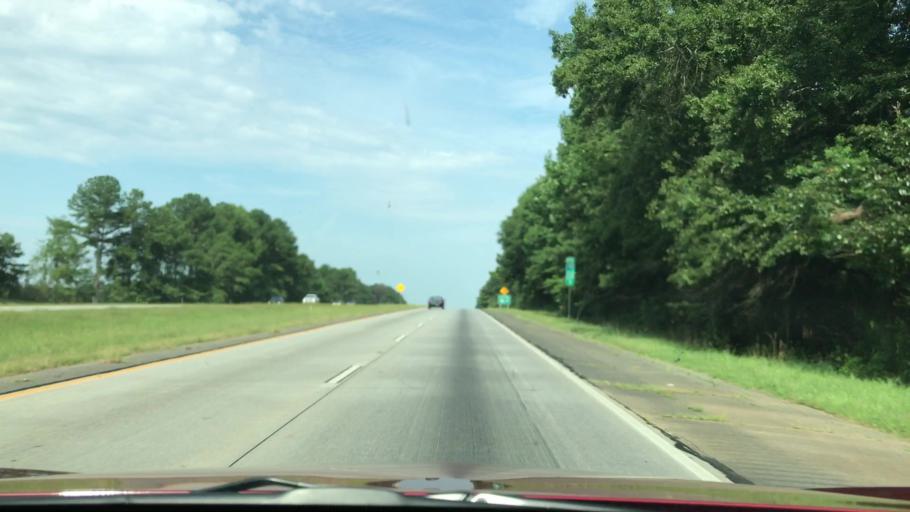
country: US
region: Georgia
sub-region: Taliaferro County
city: Crawfordville
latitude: 33.4995
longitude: -82.8005
